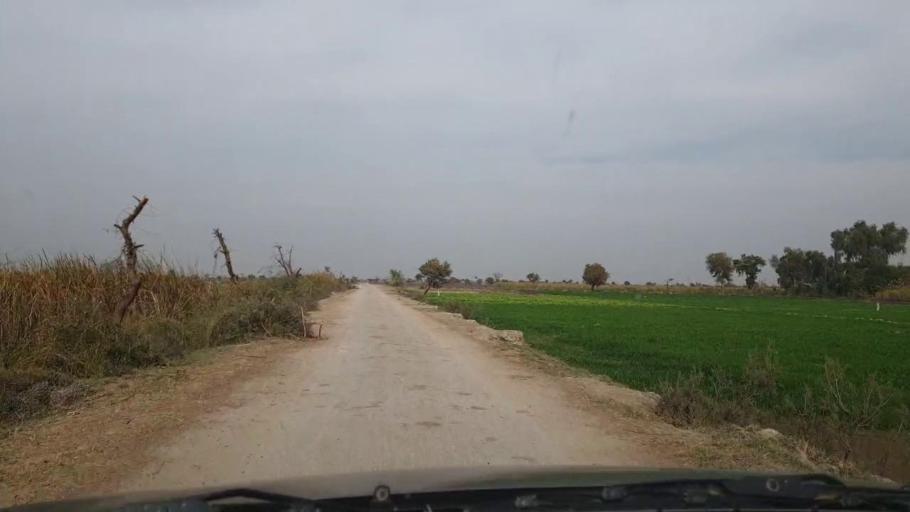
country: PK
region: Sindh
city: Sinjhoro
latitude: 26.0927
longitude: 68.8278
